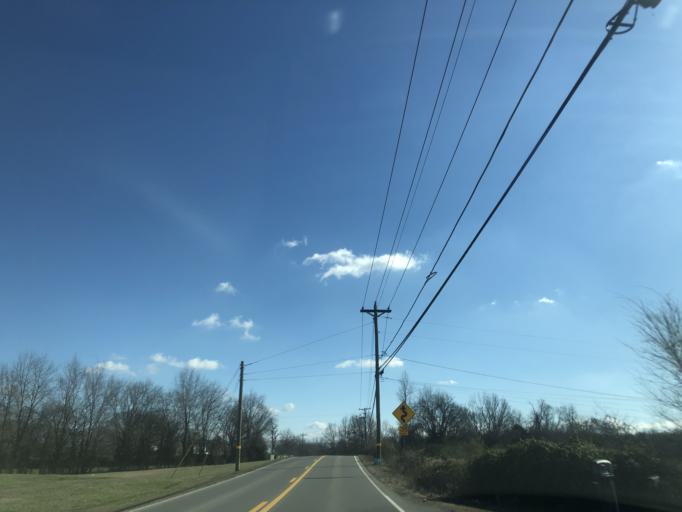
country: US
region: Tennessee
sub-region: Rutherford County
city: Murfreesboro
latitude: 35.9653
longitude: -86.3924
